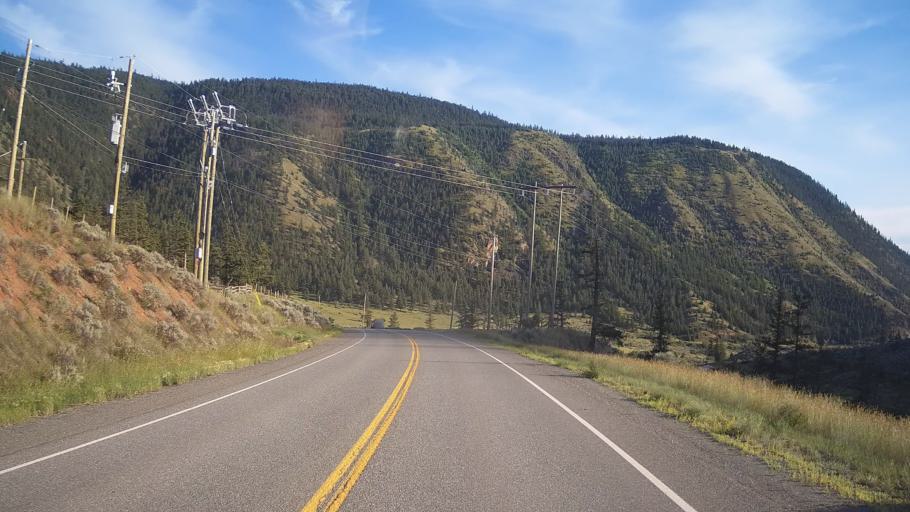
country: CA
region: British Columbia
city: Lillooet
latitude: 50.8761
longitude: -121.8322
